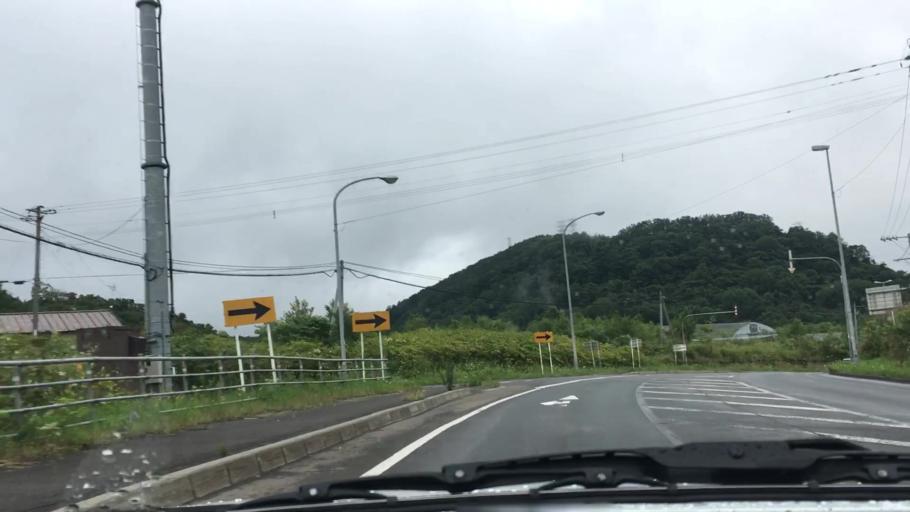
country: JP
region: Hokkaido
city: Niseko Town
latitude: 42.6074
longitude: 140.7288
